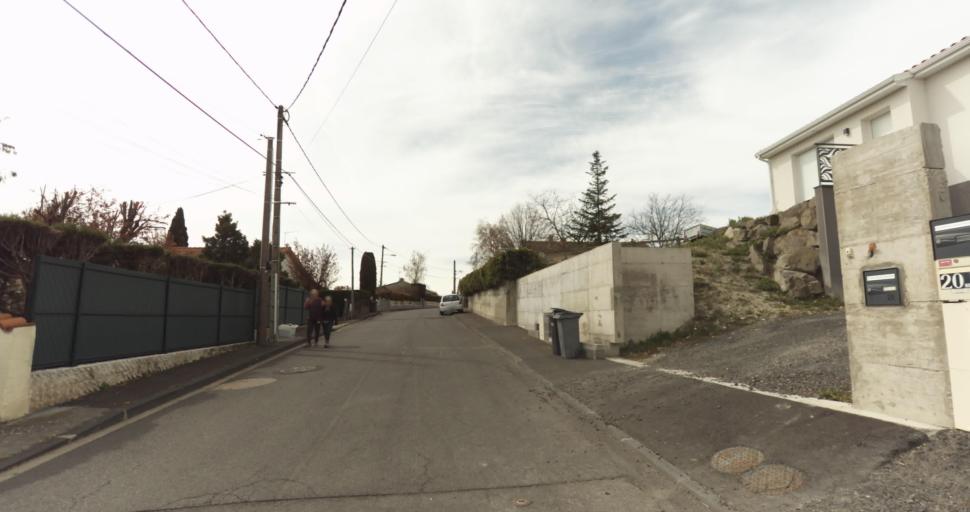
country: FR
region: Auvergne
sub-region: Departement du Puy-de-Dome
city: Cebazat
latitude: 45.8251
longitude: 3.0999
